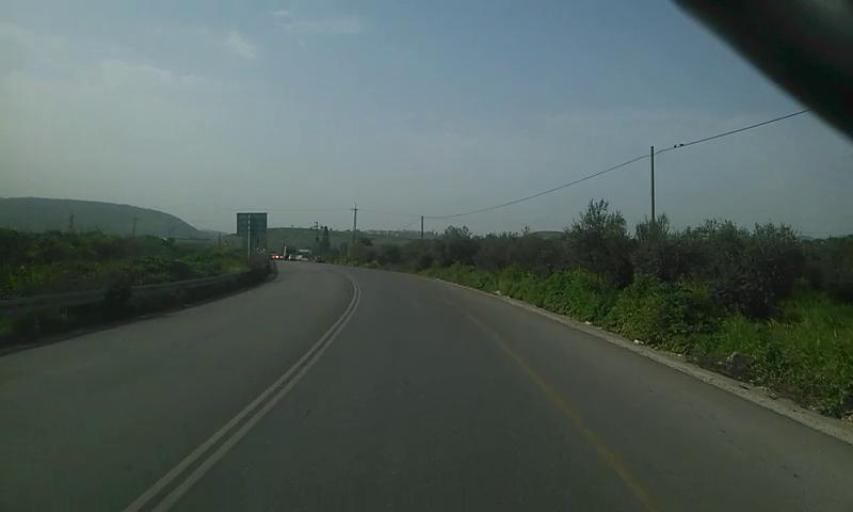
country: PS
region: West Bank
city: Dayr Sharaf
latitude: 32.2634
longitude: 35.1721
